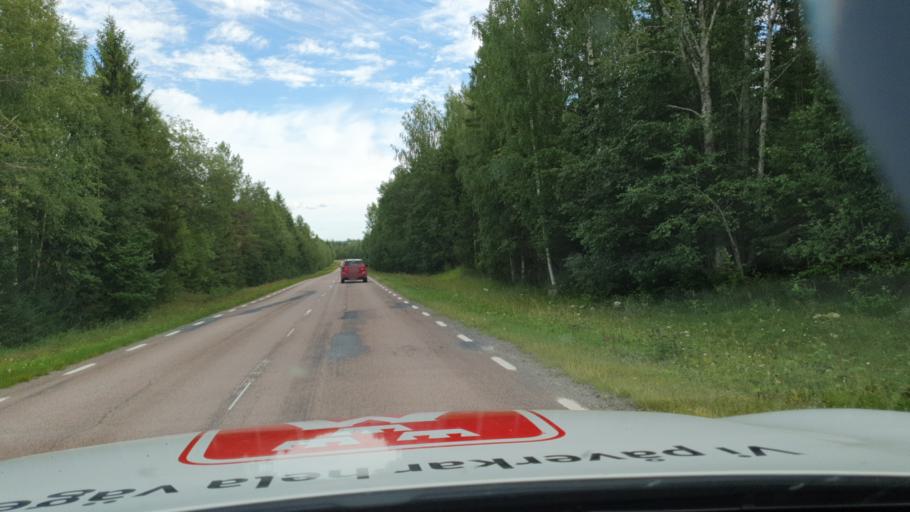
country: SE
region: Jaemtland
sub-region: Stroemsunds Kommun
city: Stroemsund
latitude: 63.6631
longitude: 15.9494
